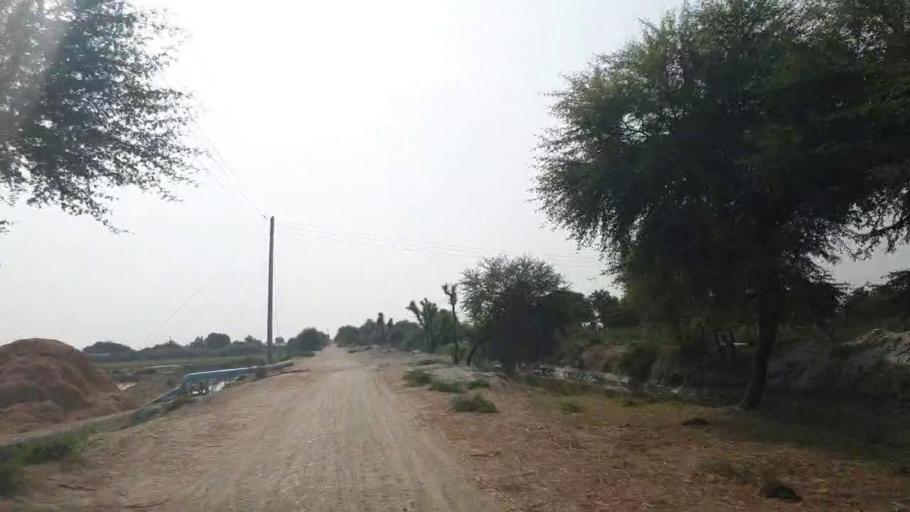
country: PK
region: Sindh
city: Badin
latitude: 24.6158
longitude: 68.7227
